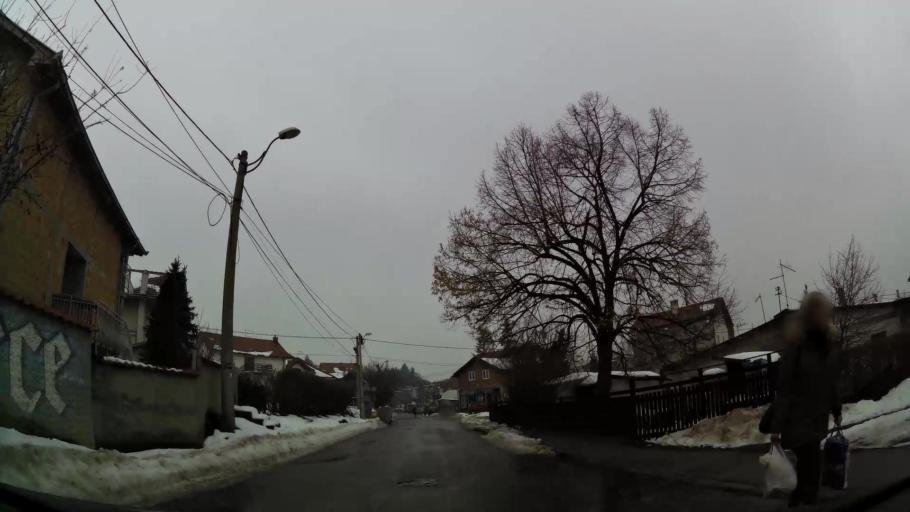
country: RS
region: Central Serbia
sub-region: Belgrade
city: Zvezdara
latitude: 44.7435
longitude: 20.5031
